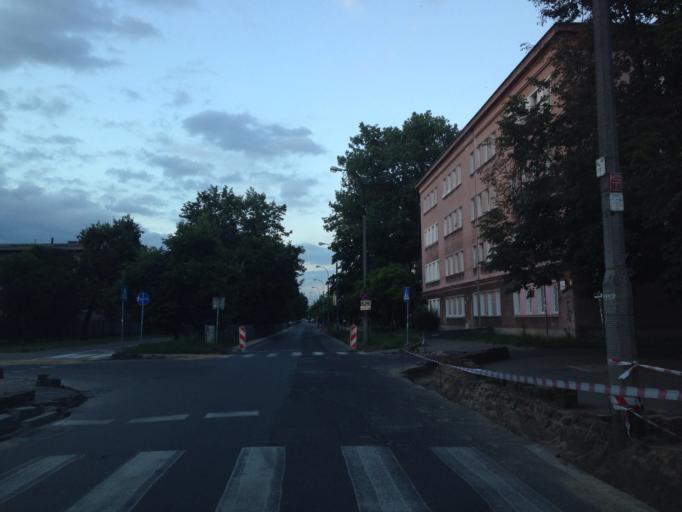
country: PL
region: Masovian Voivodeship
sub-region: Warszawa
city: Praga Polnoc
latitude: 52.2614
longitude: 21.0256
